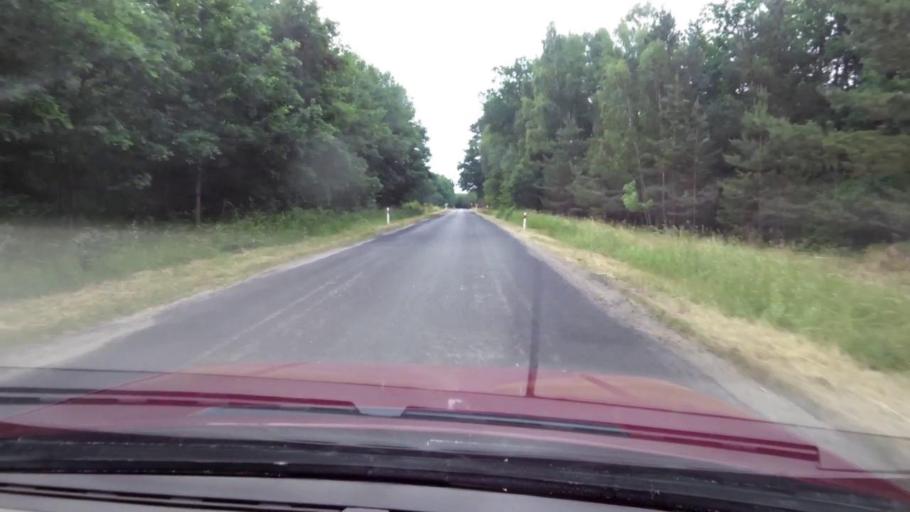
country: PL
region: Pomeranian Voivodeship
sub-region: Powiat slupski
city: Kepice
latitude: 54.2725
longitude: 16.9852
